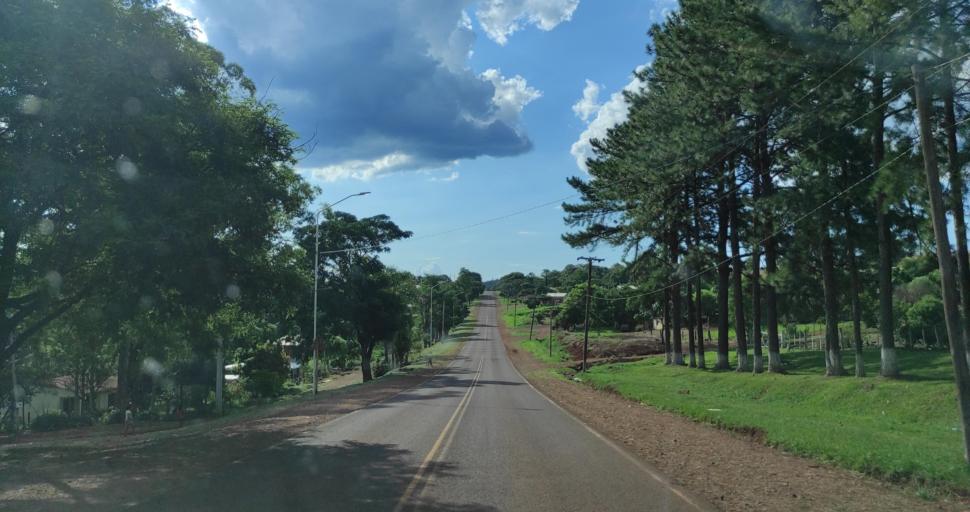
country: AR
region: Misiones
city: San Vicente
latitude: -26.3461
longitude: -54.1522
